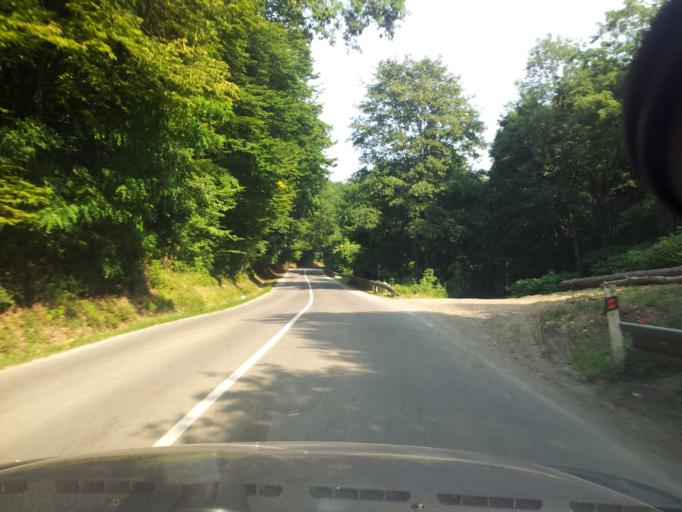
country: SK
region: Nitriansky
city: Trencianske Teplice
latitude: 48.8961
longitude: 18.1720
